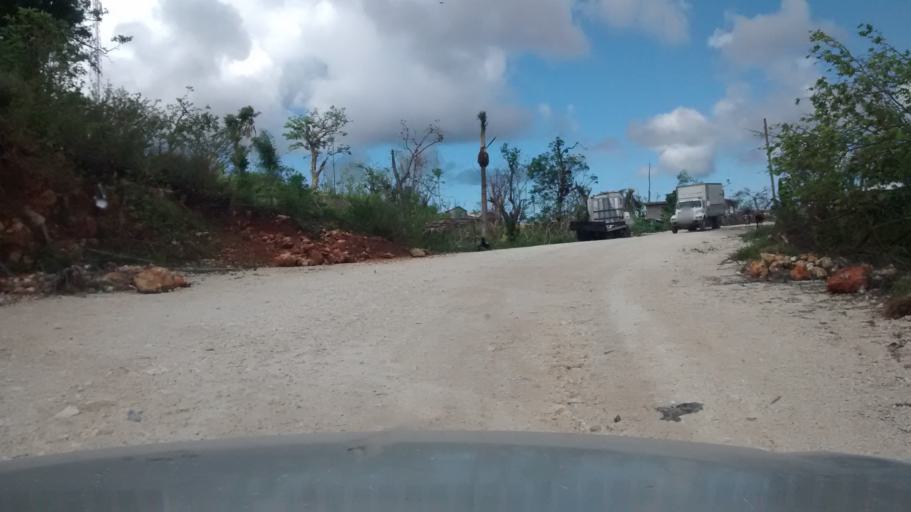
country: HT
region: Grandans
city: Corail
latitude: 18.5327
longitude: -73.9943
